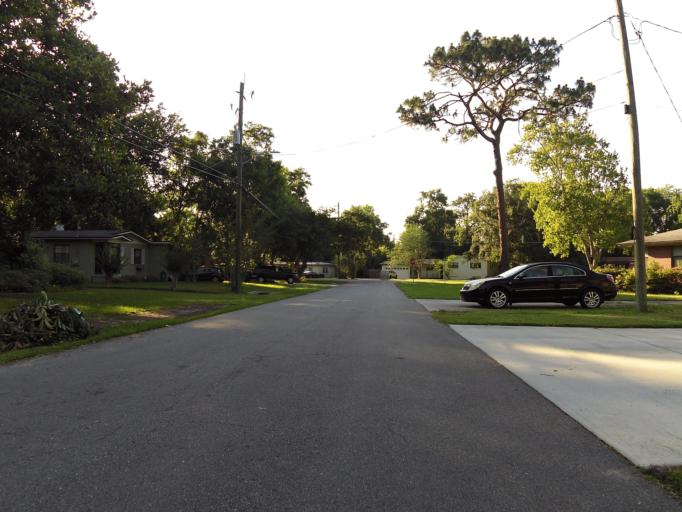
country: US
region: Florida
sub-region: Duval County
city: Jacksonville
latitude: 30.2374
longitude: -81.6189
